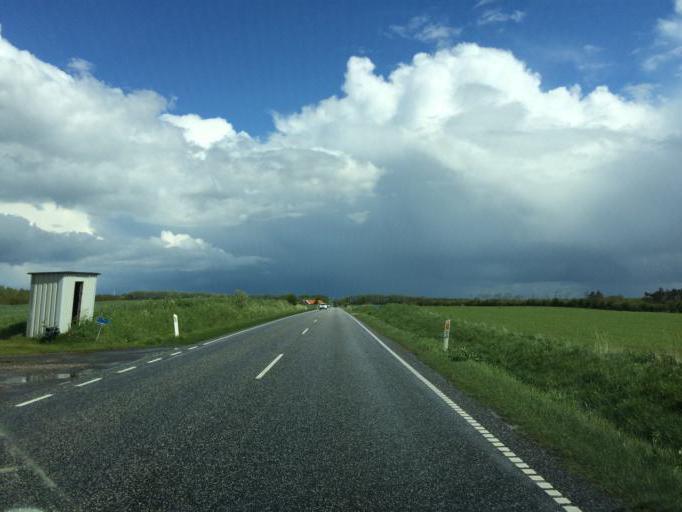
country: DK
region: Central Jutland
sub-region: Holstebro Kommune
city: Vinderup
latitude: 56.4314
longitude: 8.7139
